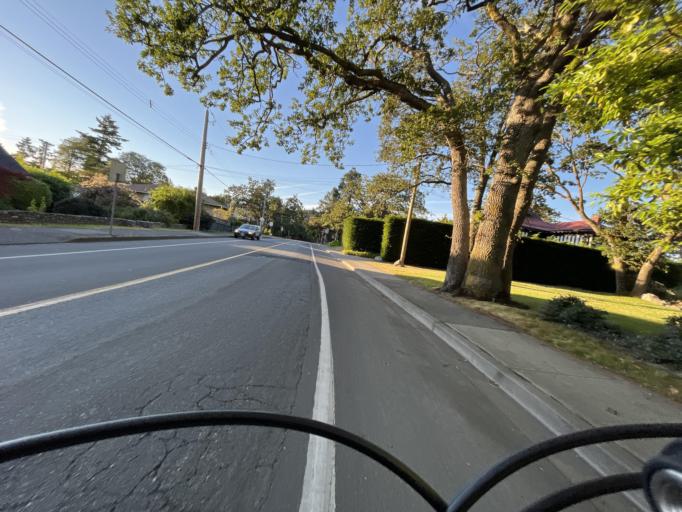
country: CA
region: British Columbia
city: Oak Bay
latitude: 48.4197
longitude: -123.3234
